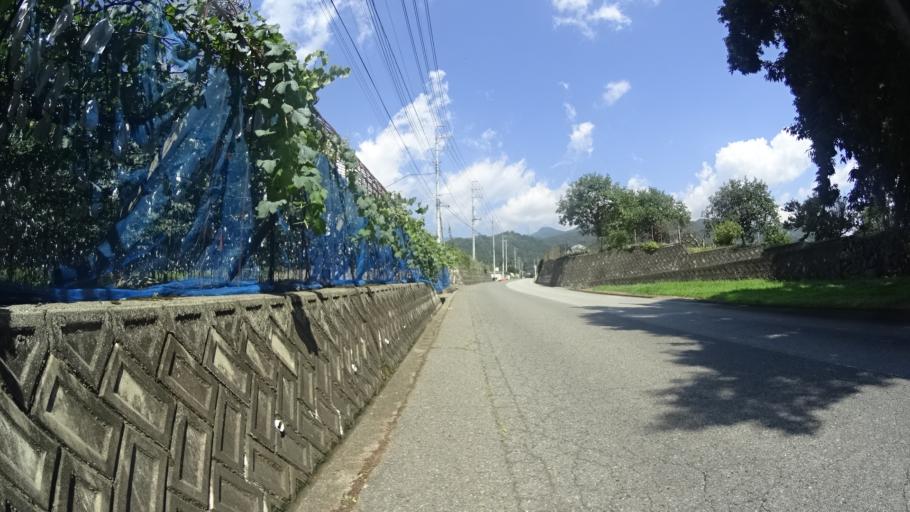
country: JP
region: Yamanashi
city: Enzan
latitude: 35.7458
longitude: 138.7188
